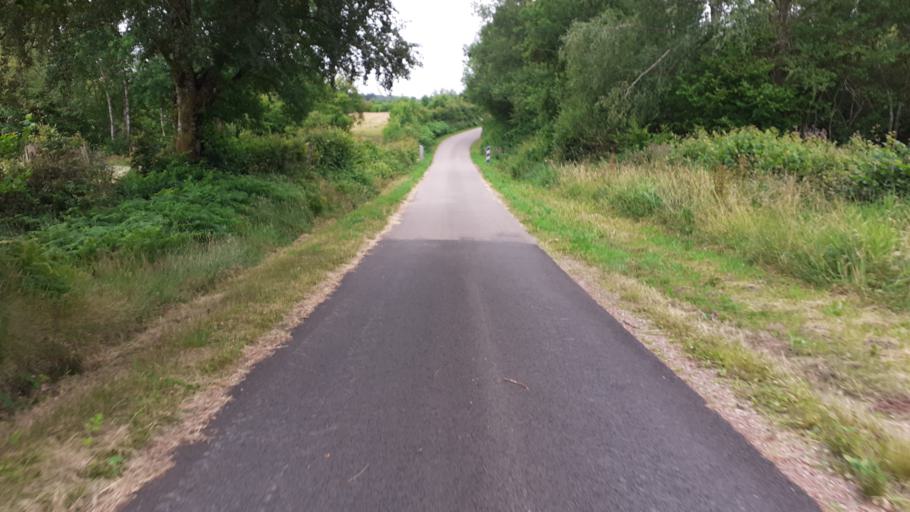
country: FR
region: Bourgogne
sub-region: Departement de la Cote-d'Or
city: Saulieu
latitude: 47.2727
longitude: 4.1331
